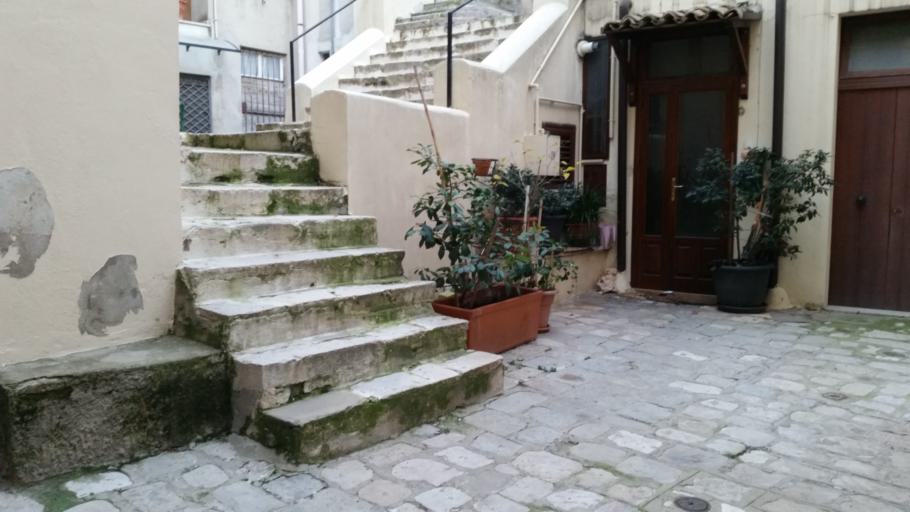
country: IT
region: Basilicate
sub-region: Provincia di Matera
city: Tricarico
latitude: 40.6229
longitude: 16.1440
